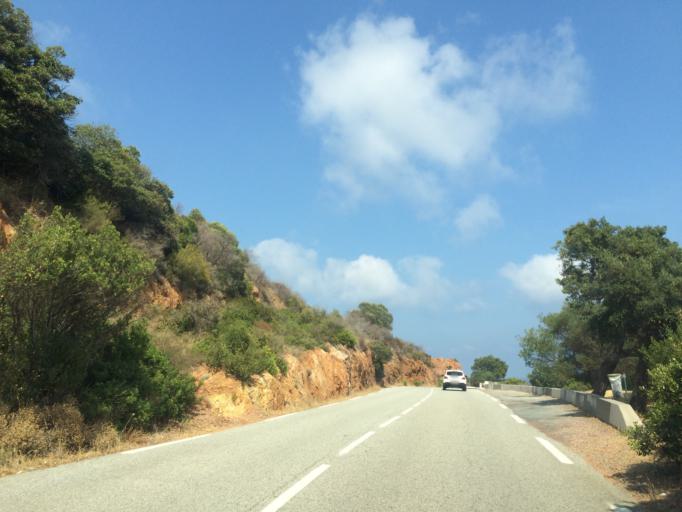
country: FR
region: Provence-Alpes-Cote d'Azur
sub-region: Departement des Alpes-Maritimes
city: Theoule-sur-Mer
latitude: 43.4458
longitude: 6.9040
